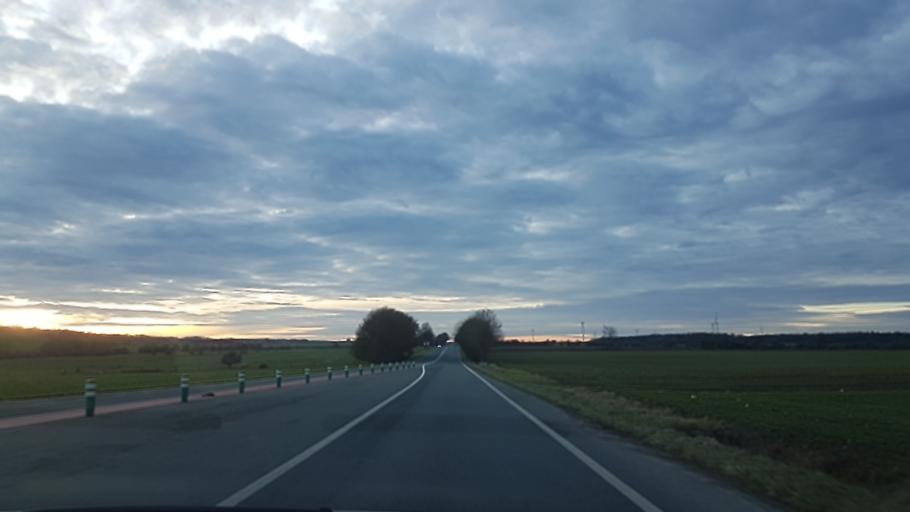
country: BE
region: Wallonia
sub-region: Province de Namur
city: Couvin
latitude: 50.0446
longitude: 4.4267
